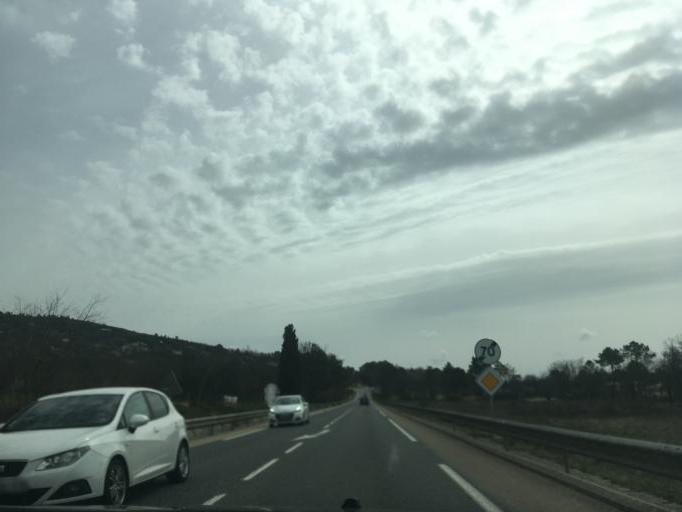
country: FR
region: Provence-Alpes-Cote d'Azur
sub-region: Departement du Var
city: Montauroux
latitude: 43.6014
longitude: 6.7799
